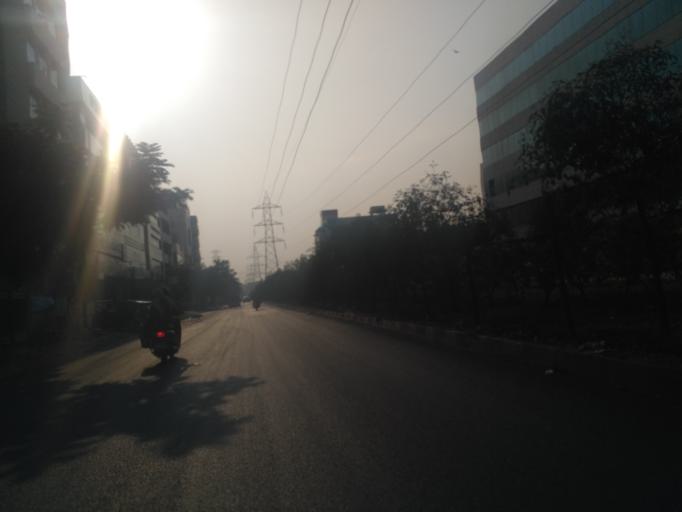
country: IN
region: Telangana
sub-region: Rangareddi
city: Kukatpalli
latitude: 17.4519
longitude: 78.3928
